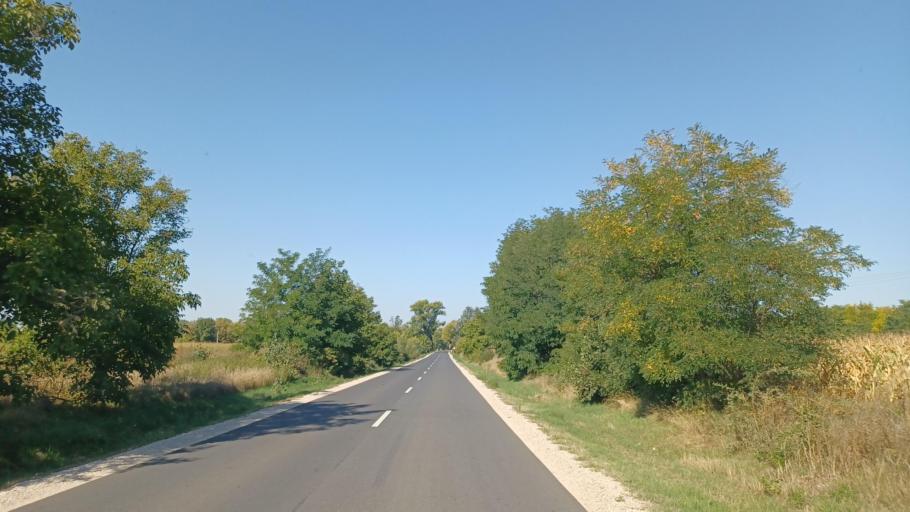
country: HU
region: Fejer
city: Cece
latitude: 46.7623
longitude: 18.6473
